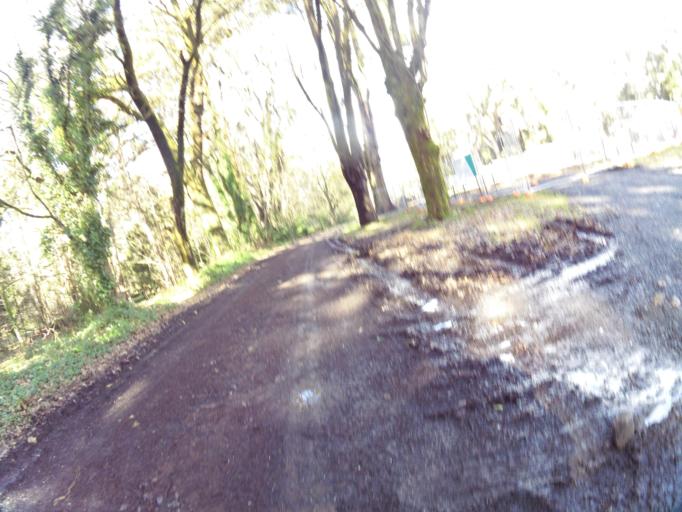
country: AU
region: Victoria
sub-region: Mount Alexander
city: Castlemaine
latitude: -37.3955
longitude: 144.2249
